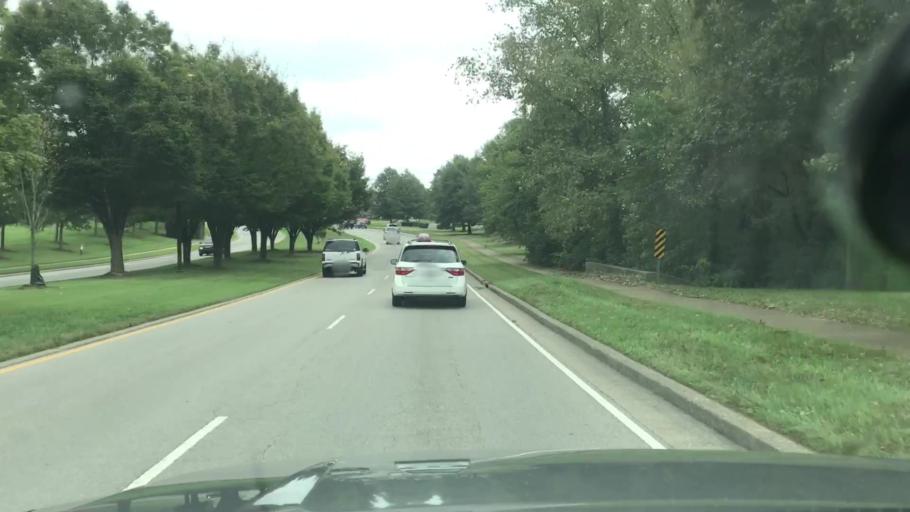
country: US
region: Tennessee
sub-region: Williamson County
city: Franklin
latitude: 35.9409
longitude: -86.8356
